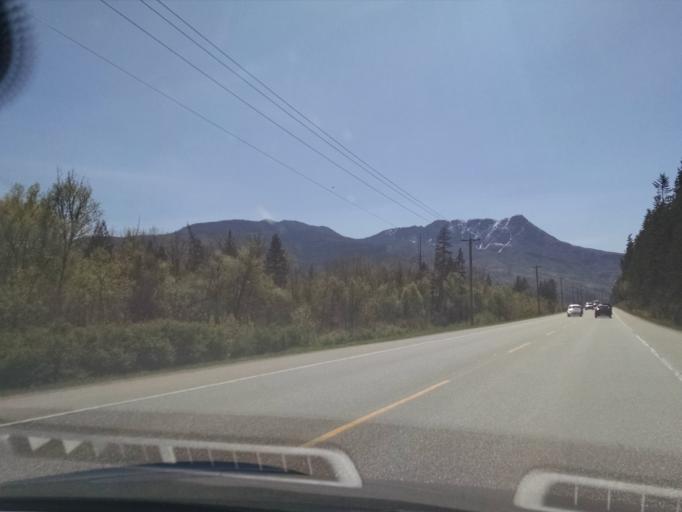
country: CA
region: British Columbia
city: Salmon Arm
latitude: 50.7199
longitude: -119.3176
